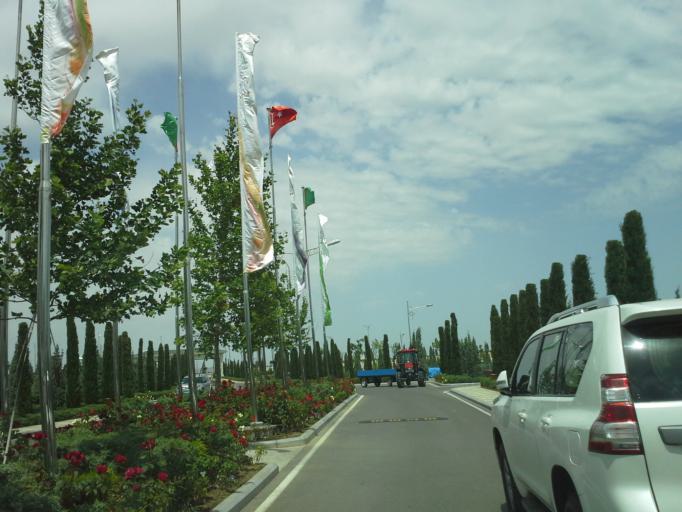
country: TM
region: Balkan
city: Turkmenbasy
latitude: 39.9461
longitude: 52.8788
